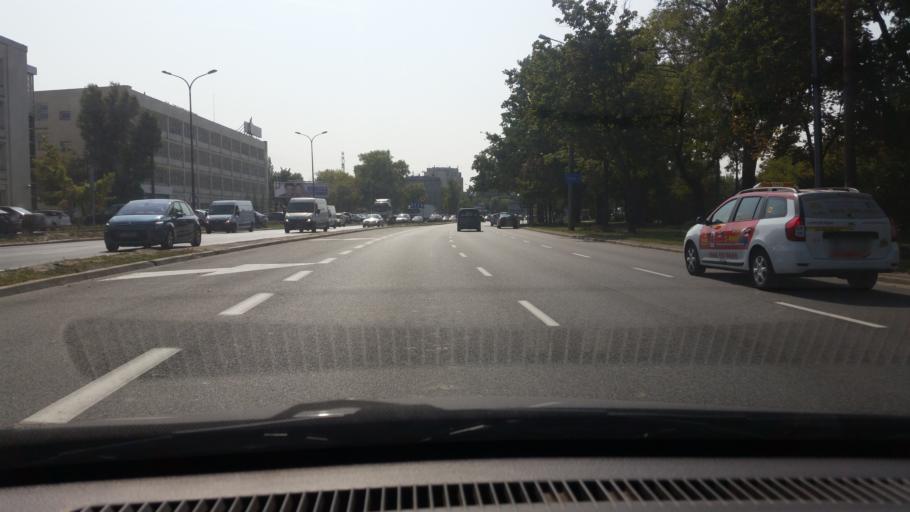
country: PL
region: Masovian Voivodeship
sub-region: Warszawa
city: Praga Polnoc
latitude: 52.2680
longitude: 21.0198
